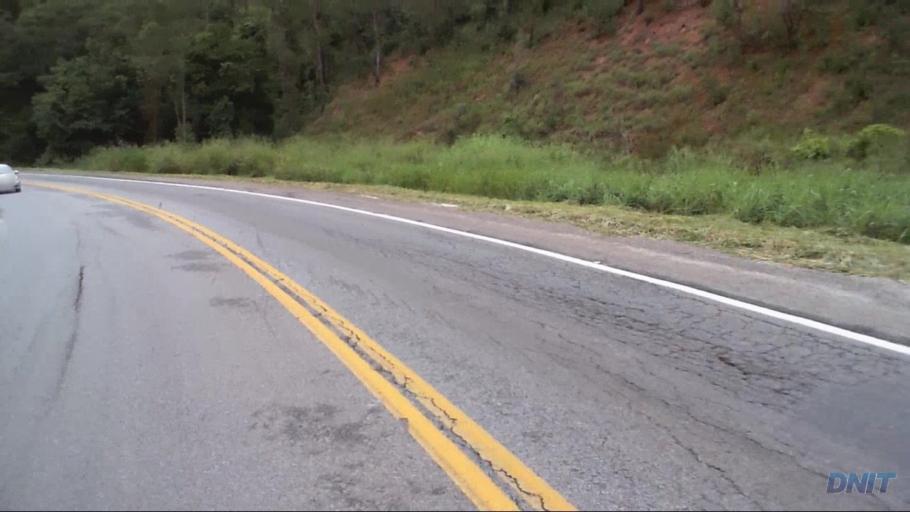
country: BR
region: Minas Gerais
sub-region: Joao Monlevade
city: Joao Monlevade
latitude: -19.8551
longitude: -43.2646
